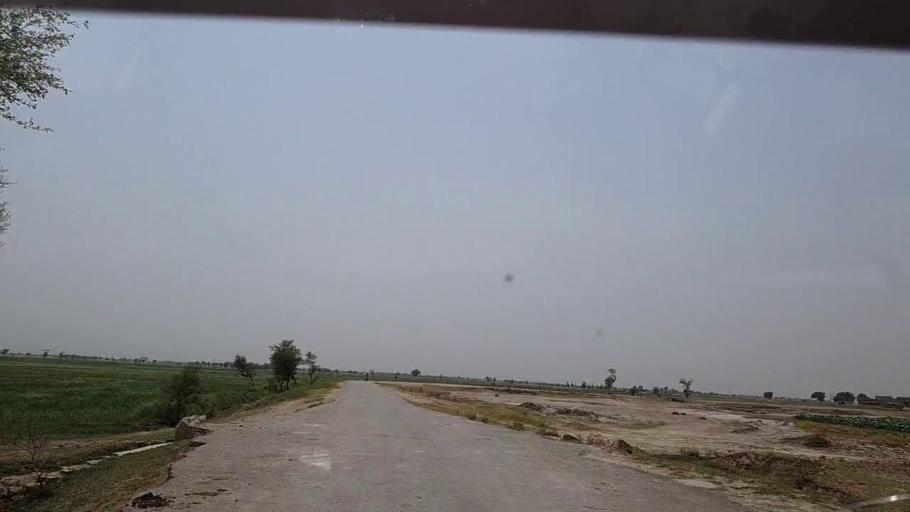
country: PK
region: Sindh
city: Khairpur Nathan Shah
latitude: 27.0183
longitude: 67.6632
